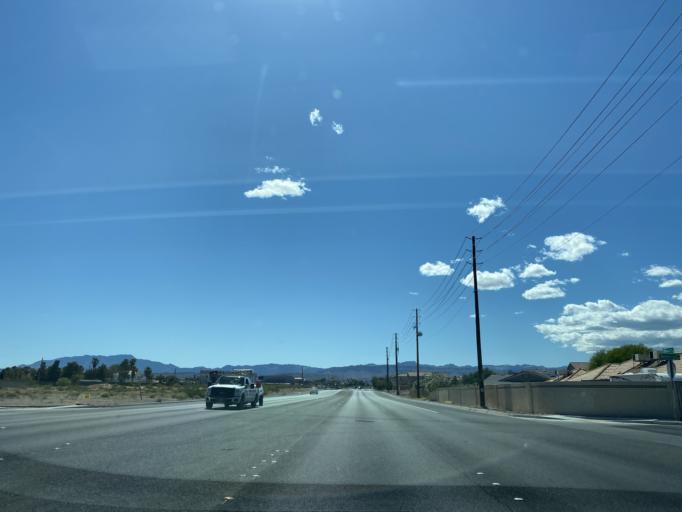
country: US
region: Nevada
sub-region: Clark County
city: Spring Valley
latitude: 36.0857
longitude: -115.2206
